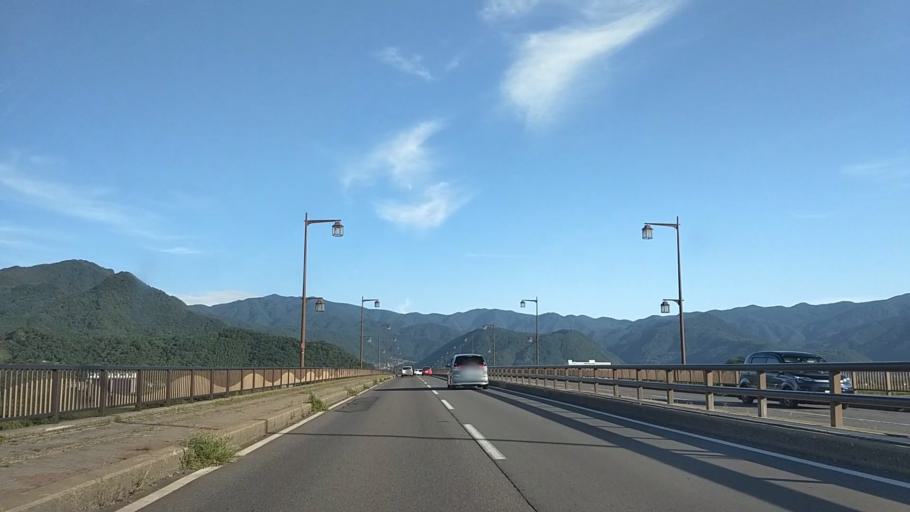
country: JP
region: Nagano
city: Nagano-shi
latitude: 36.5830
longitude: 138.1913
